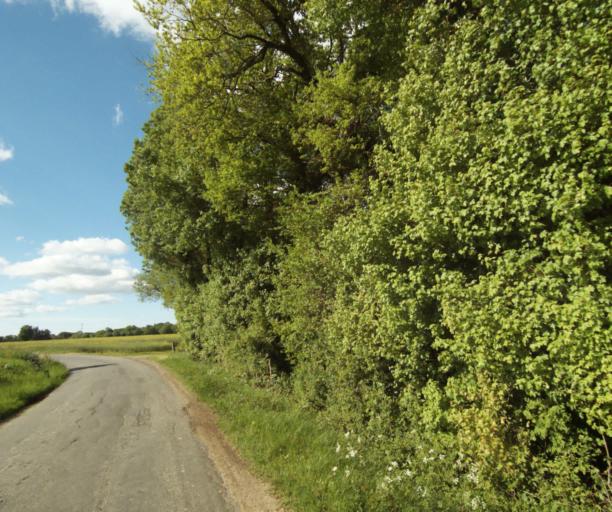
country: FR
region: Poitou-Charentes
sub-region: Departement de la Charente-Maritime
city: Nieul-les-Saintes
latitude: 45.7045
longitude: -0.7382
